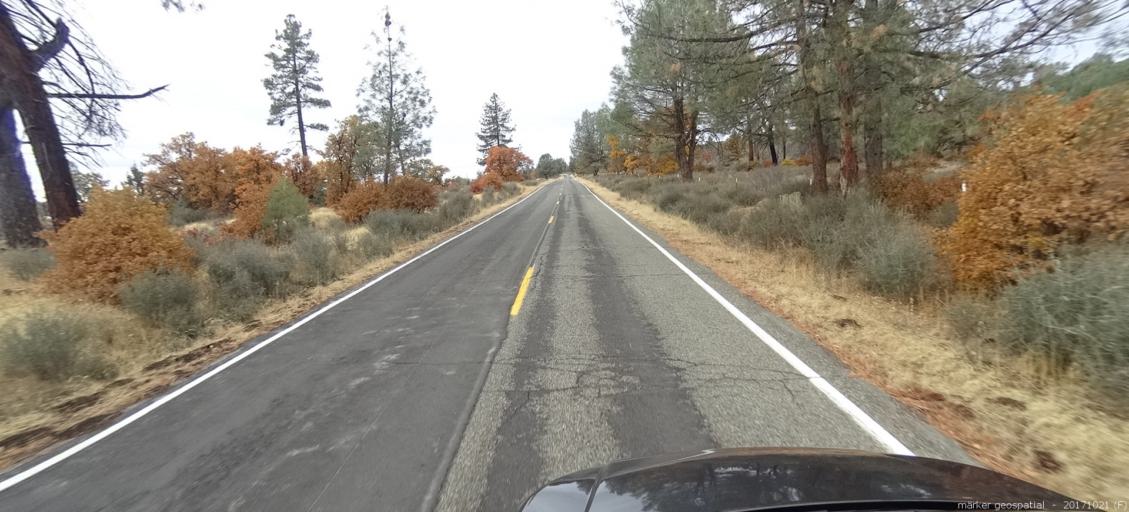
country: US
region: California
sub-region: Shasta County
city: Burney
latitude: 40.9426
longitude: -121.4432
